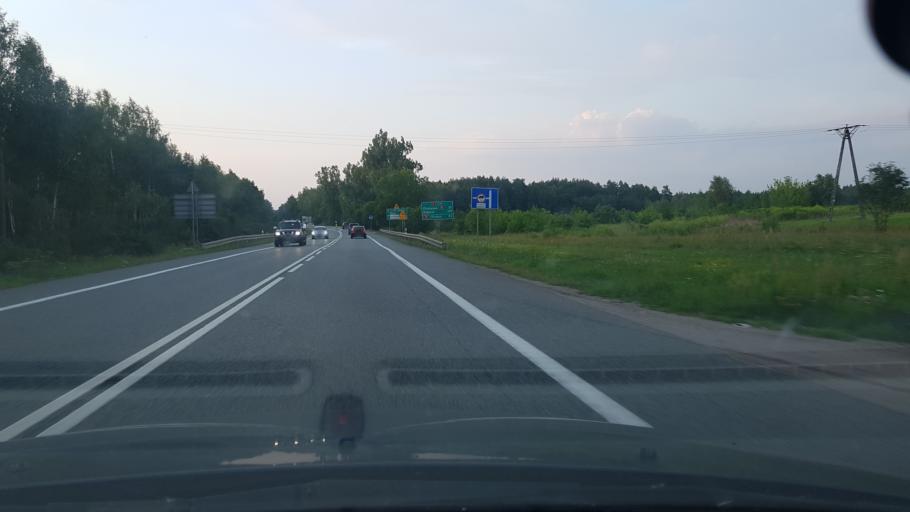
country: PL
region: Masovian Voivodeship
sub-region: Powiat mlawski
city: Mlawa
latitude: 53.1302
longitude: 20.3944
